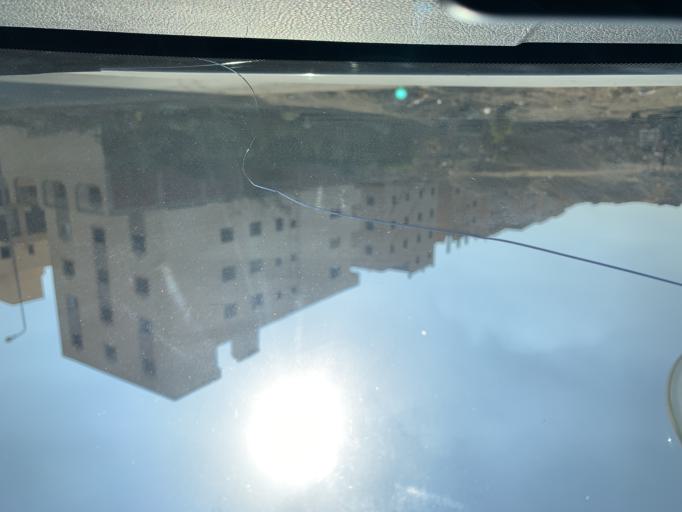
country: EG
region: Muhafazat al Qalyubiyah
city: Al Khankah
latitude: 30.0187
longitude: 31.4779
